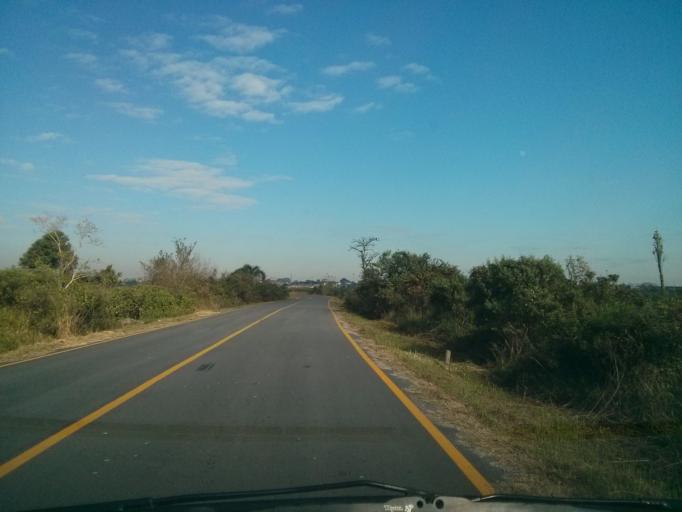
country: BR
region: Parana
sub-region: Sao Jose Dos Pinhais
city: Sao Jose dos Pinhais
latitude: -25.5292
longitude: -49.2222
